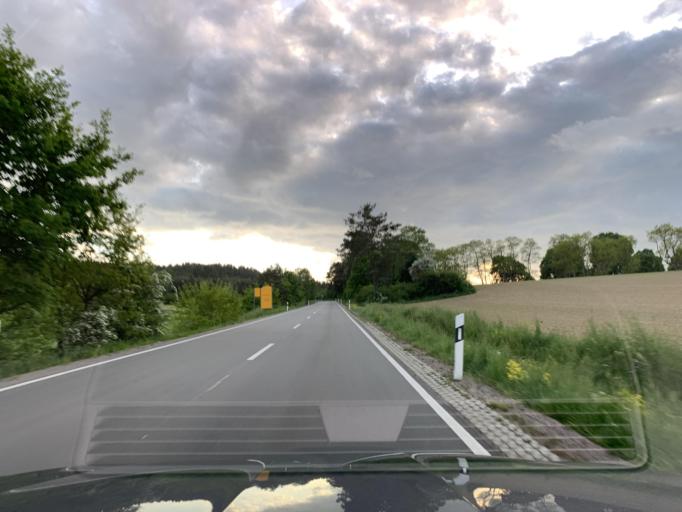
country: DE
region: Bavaria
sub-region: Upper Palatinate
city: Pettendorf
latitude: 49.3431
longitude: 12.3668
